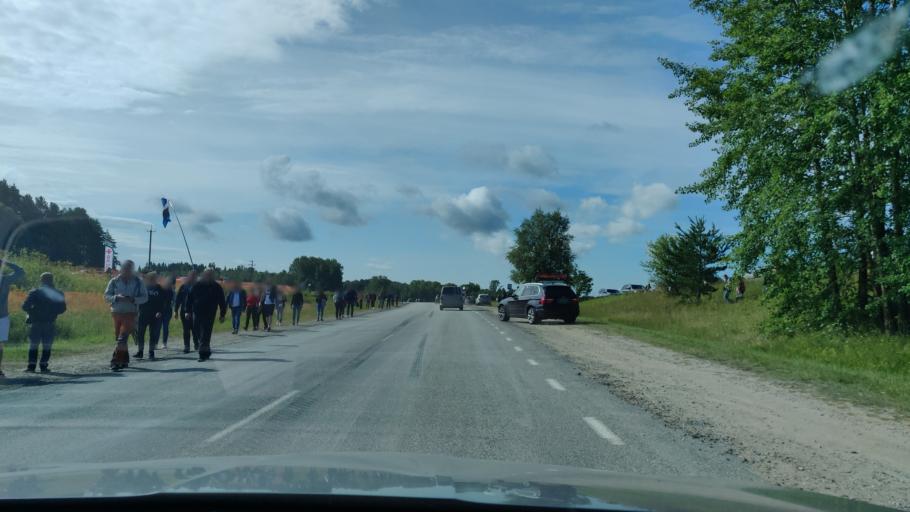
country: EE
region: Tartu
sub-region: Elva linn
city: Elva
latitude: 58.1373
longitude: 26.5207
